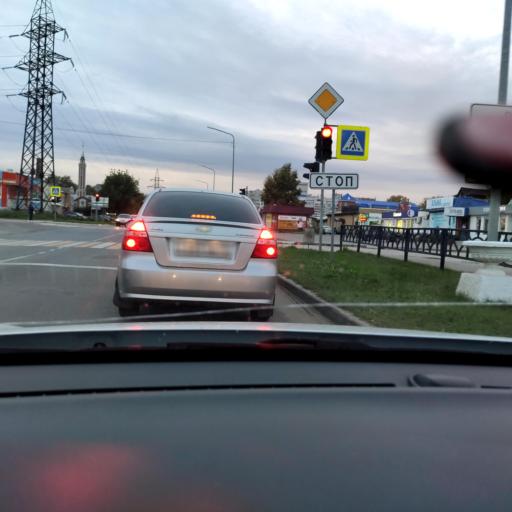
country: RU
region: Mariy-El
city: Volzhsk
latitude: 55.8651
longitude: 48.3603
